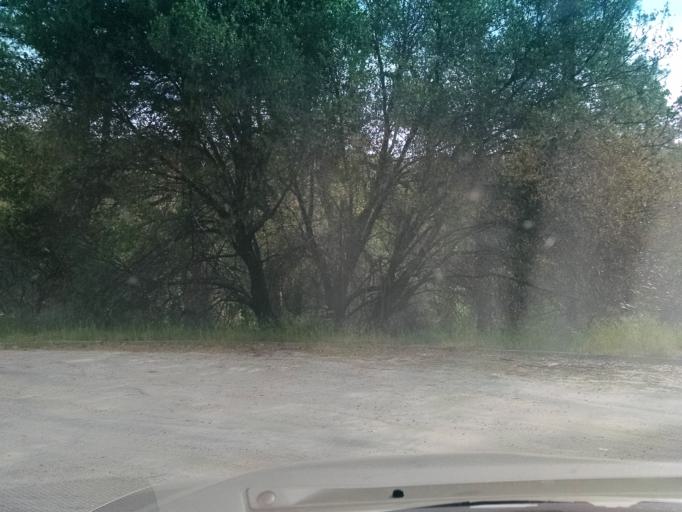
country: US
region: California
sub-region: Madera County
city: Oakhurst
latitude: 37.3230
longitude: -119.6288
